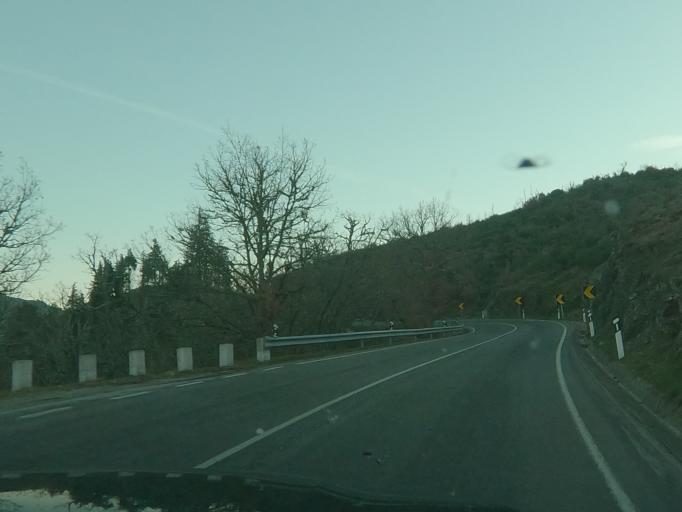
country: PT
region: Vila Real
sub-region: Vila Pouca de Aguiar
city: Vila Pouca de Aguiar
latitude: 41.4160
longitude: -7.6871
